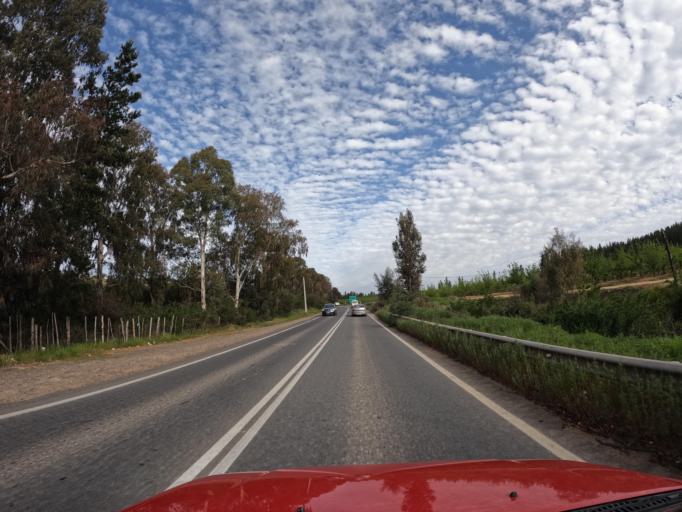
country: CL
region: O'Higgins
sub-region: Provincia de Colchagua
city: Santa Cruz
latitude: -34.3278
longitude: -71.7524
